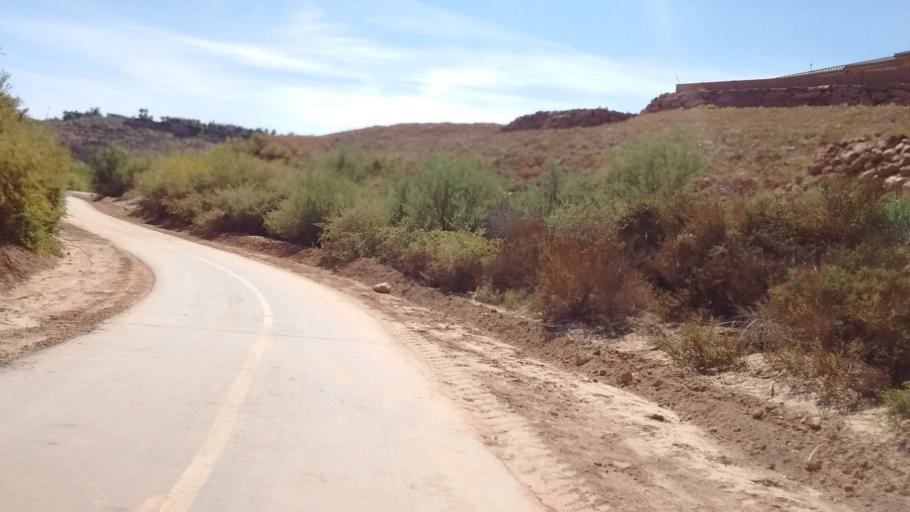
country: US
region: Utah
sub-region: Washington County
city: Saint George
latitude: 37.0880
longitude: -113.5407
